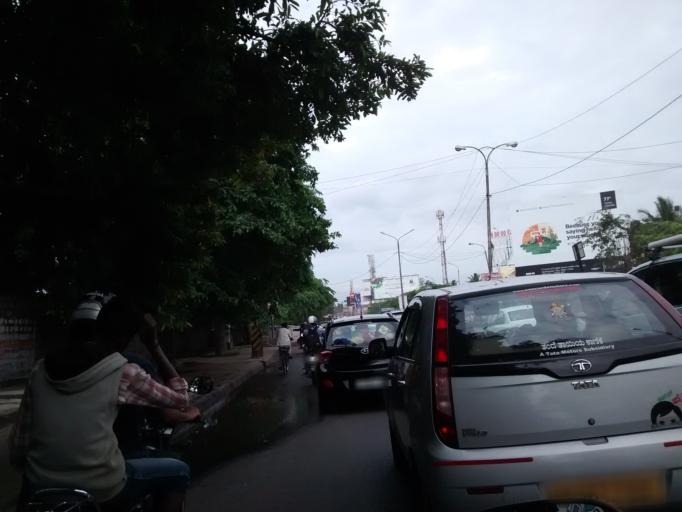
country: IN
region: Karnataka
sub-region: Bangalore Urban
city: Bangalore
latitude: 12.9554
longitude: 77.6892
